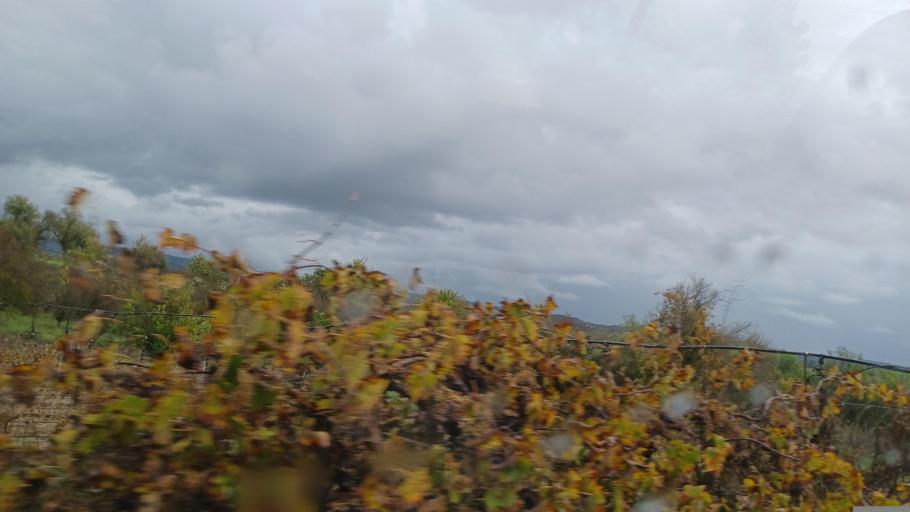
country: CY
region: Pafos
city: Mesogi
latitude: 34.8587
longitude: 32.5392
